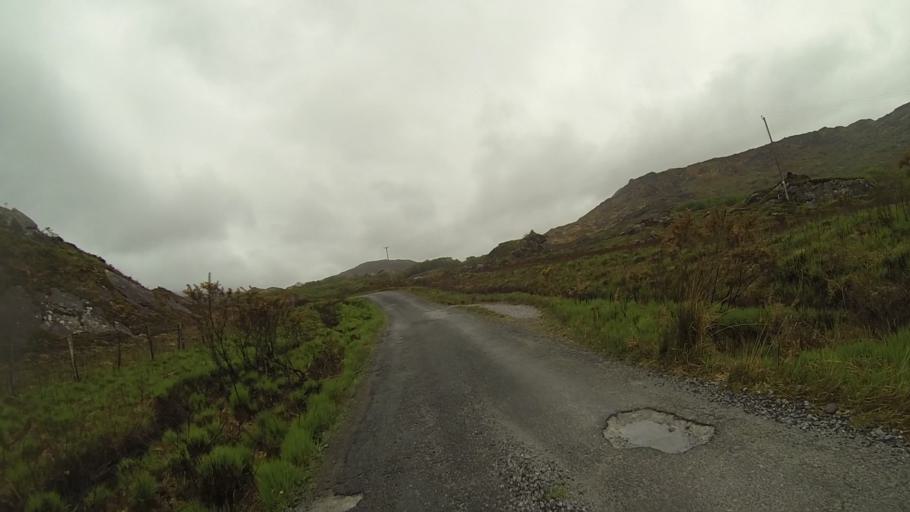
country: IE
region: Munster
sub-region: Ciarrai
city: Kenmare
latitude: 51.9693
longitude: -9.6365
